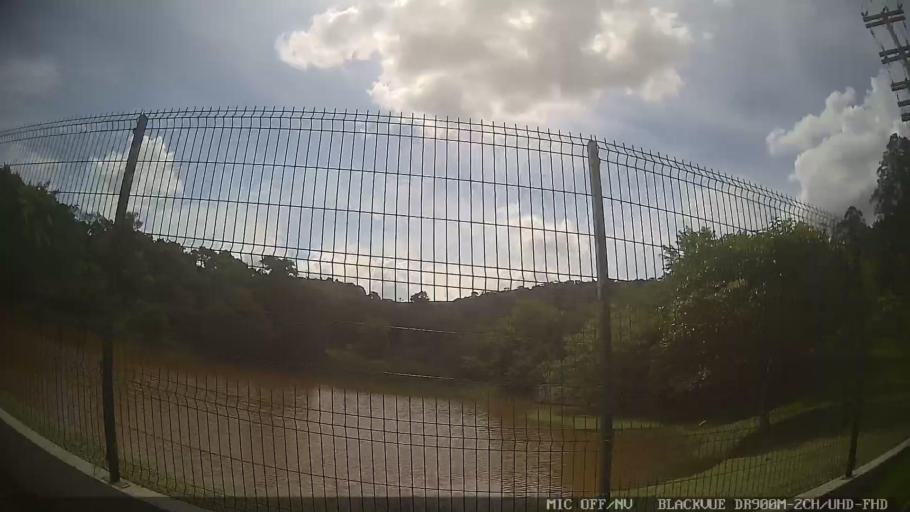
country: BR
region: Sao Paulo
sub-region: Atibaia
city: Atibaia
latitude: -23.0822
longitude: -46.5516
